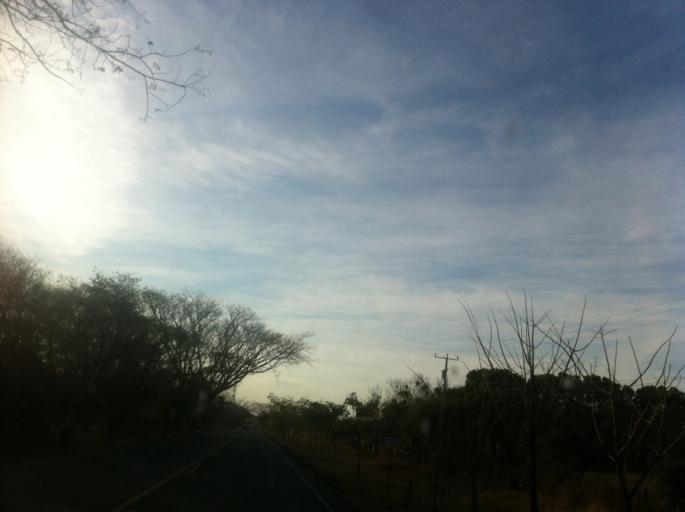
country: NI
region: Rivas
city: Rivas
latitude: 11.3767
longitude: -85.7612
